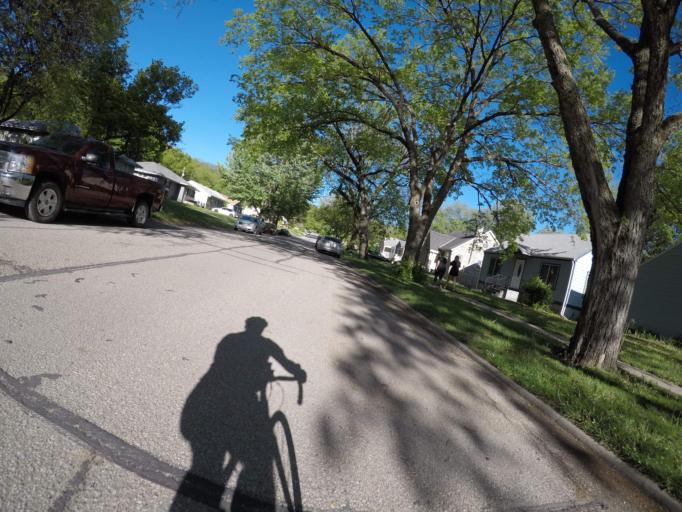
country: US
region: Kansas
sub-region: Riley County
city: Manhattan
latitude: 39.1919
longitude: -96.5694
